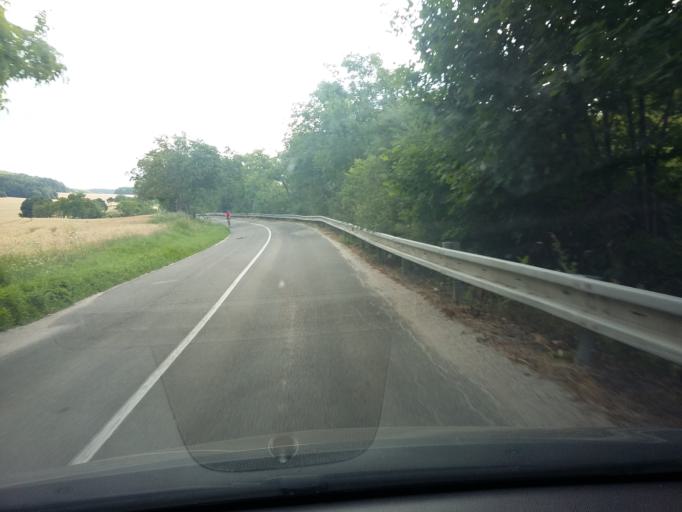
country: SK
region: Trnavsky
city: Smolenice
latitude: 48.5364
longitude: 17.3584
